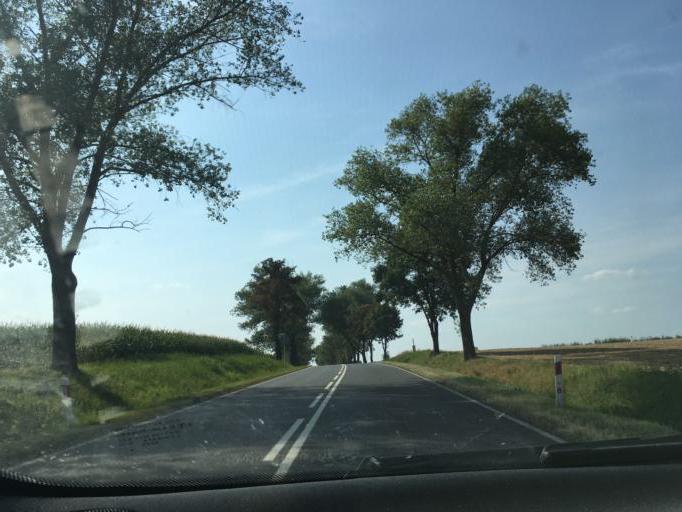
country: PL
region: Opole Voivodeship
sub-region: Powiat prudnicki
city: Moszczanka
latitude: 50.4208
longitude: 17.4655
